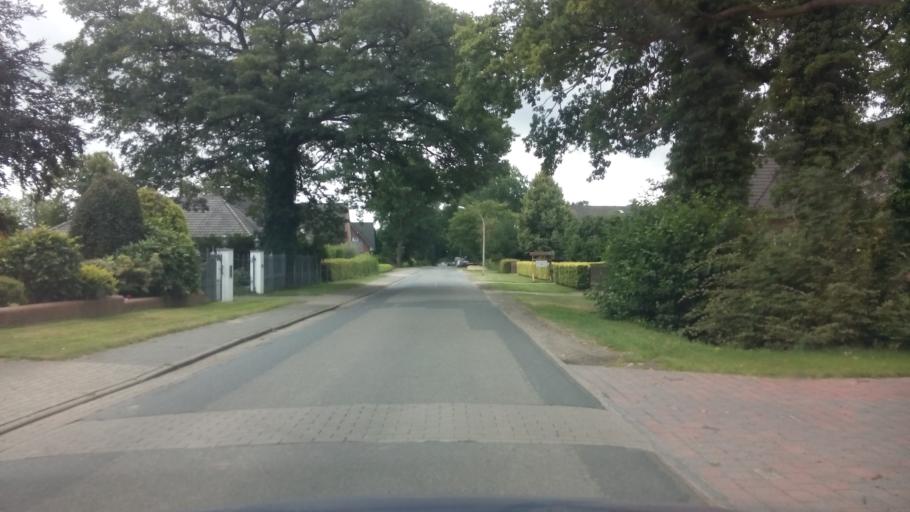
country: DE
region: Lower Saxony
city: Ritterhude
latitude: 53.2147
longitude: 8.7509
